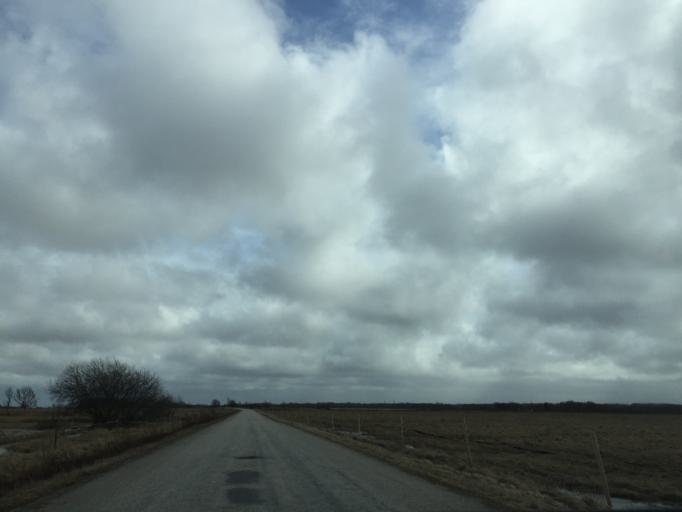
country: EE
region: Laeaene
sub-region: Lihula vald
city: Lihula
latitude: 58.7297
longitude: 23.8812
